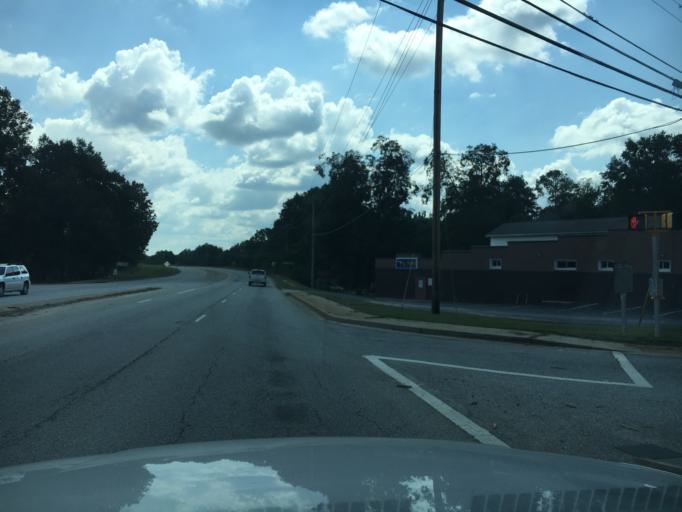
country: US
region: South Carolina
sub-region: Greenwood County
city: Greenwood
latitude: 34.1815
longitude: -82.1839
